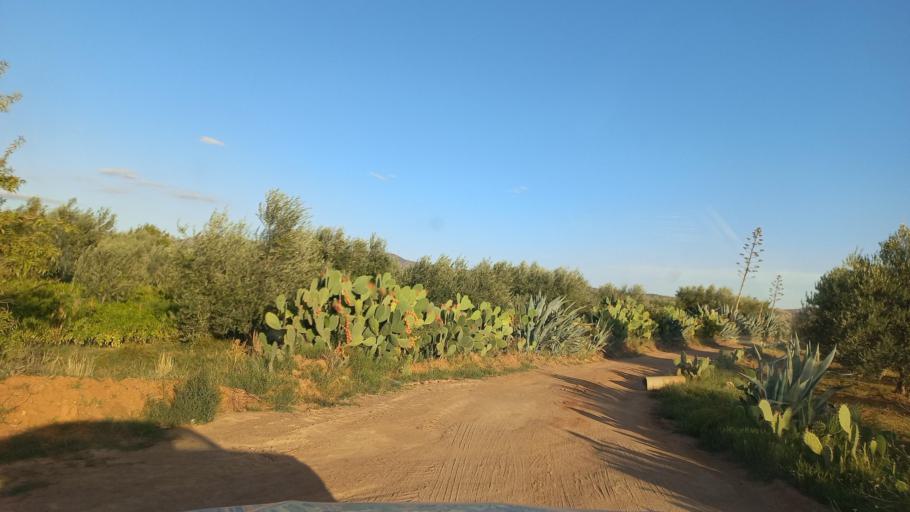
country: TN
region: Al Qasrayn
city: Sbiba
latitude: 35.4192
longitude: 9.1342
